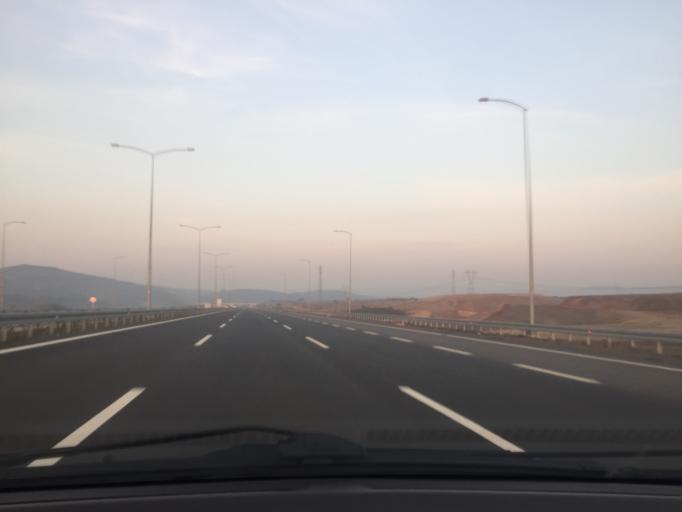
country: TR
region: Bursa
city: Mahmudiye
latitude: 40.2736
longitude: 28.5939
